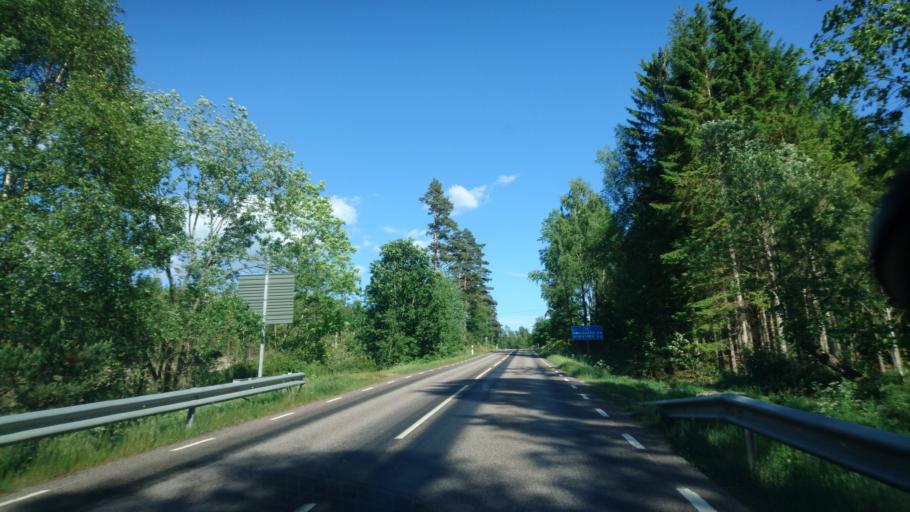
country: SE
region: Skane
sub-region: Osby Kommun
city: Lonsboda
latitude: 56.3919
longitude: 14.3370
